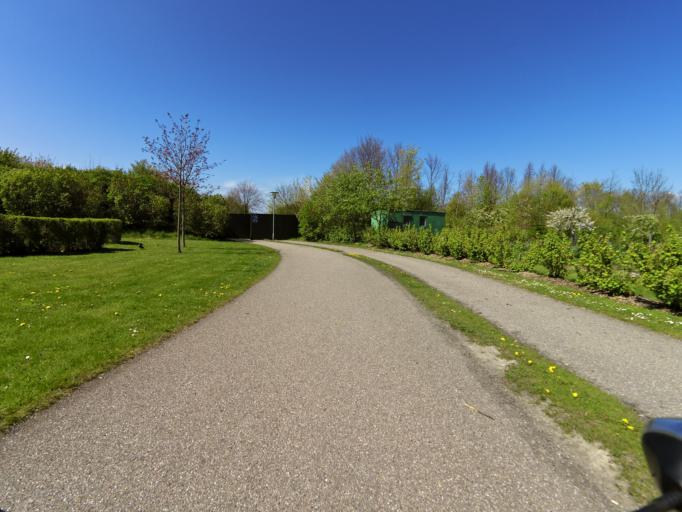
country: DK
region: Capital Region
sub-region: Hoje-Taastrup Kommune
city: Taastrup
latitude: 55.6380
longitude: 12.2666
